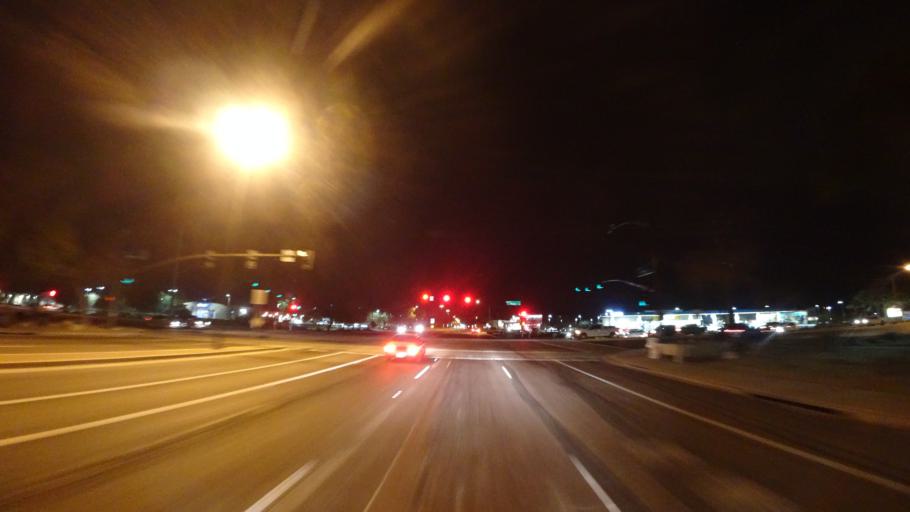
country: US
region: Arizona
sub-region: Maricopa County
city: Gilbert
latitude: 33.2928
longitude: -111.7211
